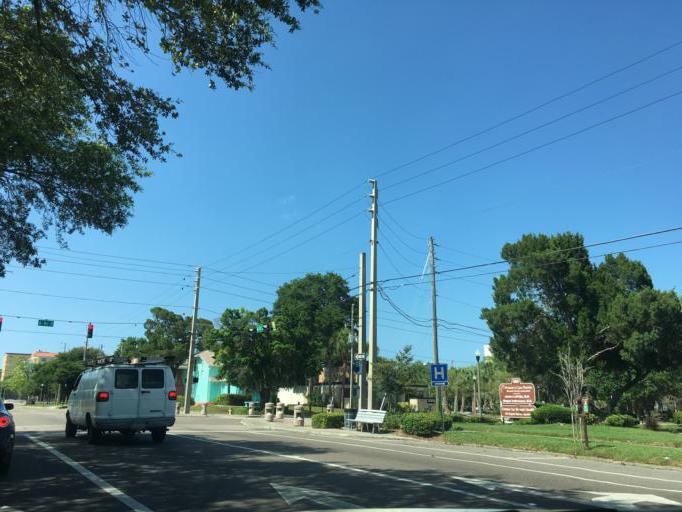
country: US
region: Florida
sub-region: Pinellas County
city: Saint Petersburg
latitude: 27.7639
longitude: -82.6448
